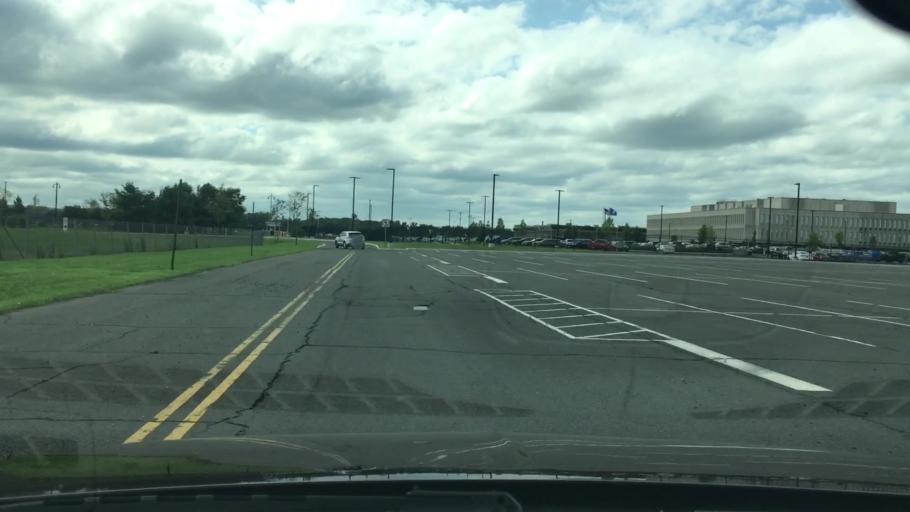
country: US
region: Connecticut
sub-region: Hartford County
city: East Hartford
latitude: 41.7571
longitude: -72.6267
